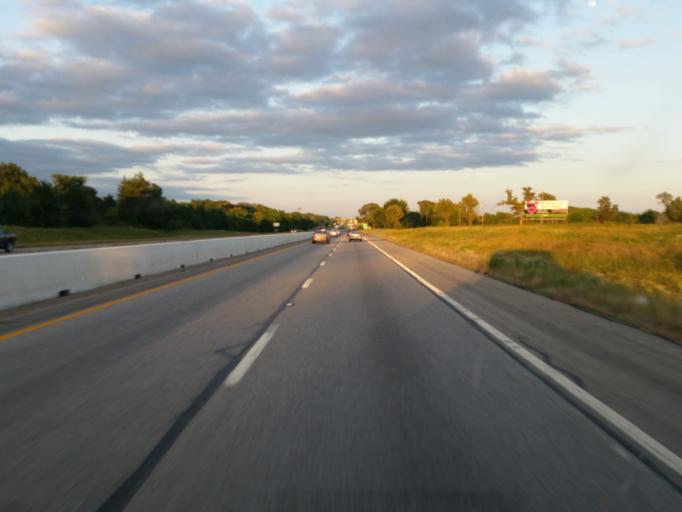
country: US
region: Texas
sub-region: Van Zandt County
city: Van
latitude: 32.5113
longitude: -95.6698
